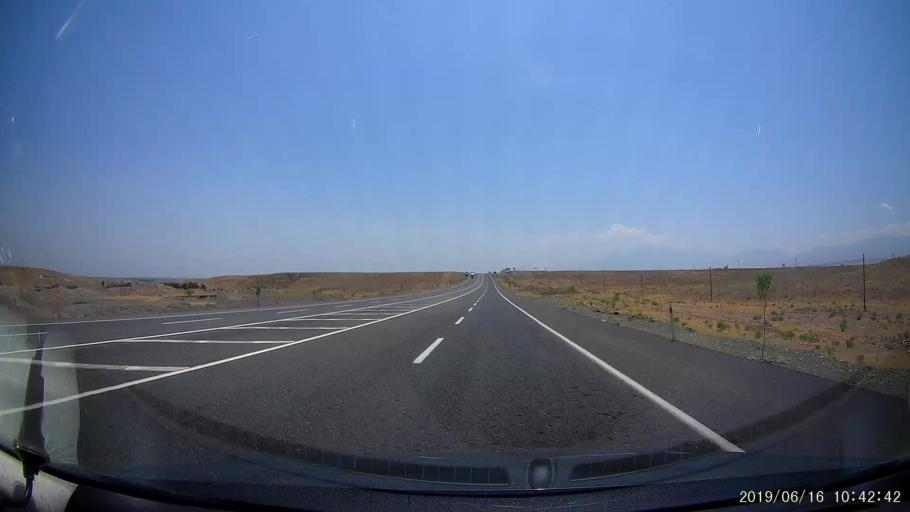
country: AM
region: Armavir
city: Shenavan
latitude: 40.0401
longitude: 43.8129
